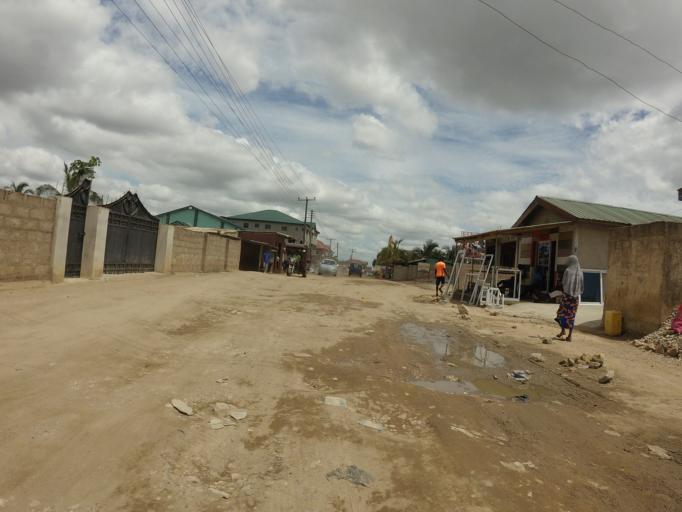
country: GH
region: Central
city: Kasoa
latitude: 5.5464
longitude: -0.3977
